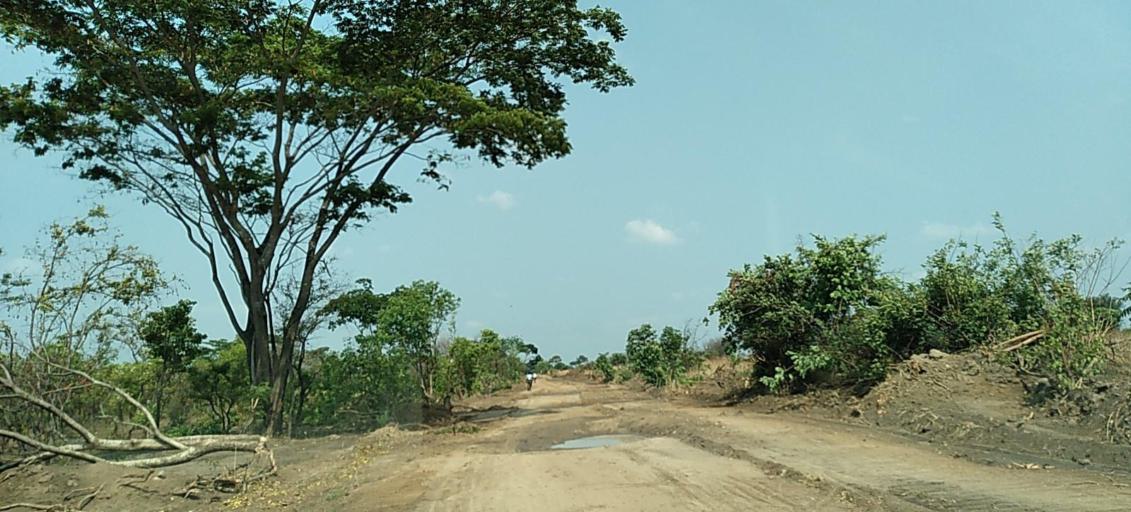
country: ZM
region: Copperbelt
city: Luanshya
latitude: -13.0897
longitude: 28.2674
